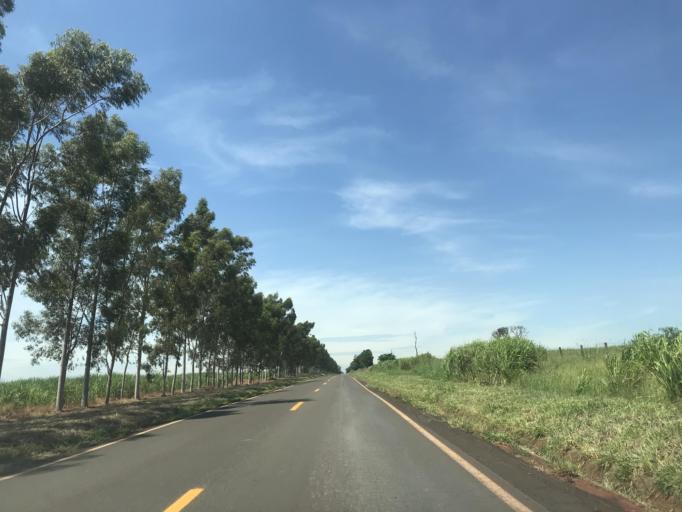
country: BR
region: Parana
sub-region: Paranavai
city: Nova Aurora
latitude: -22.8294
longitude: -52.6558
